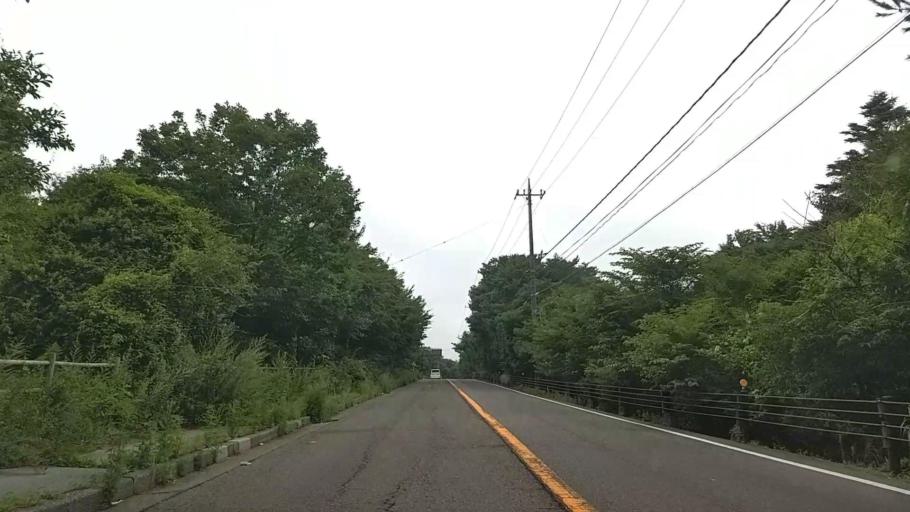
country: JP
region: Yamanashi
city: Fujikawaguchiko
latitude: 35.4493
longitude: 138.6082
